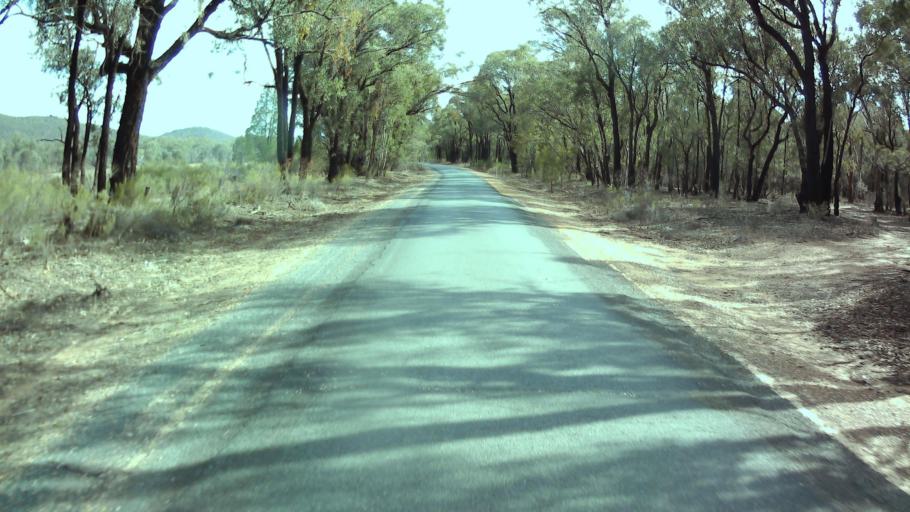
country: AU
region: New South Wales
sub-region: Weddin
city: Grenfell
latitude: -33.8606
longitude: 148.2145
